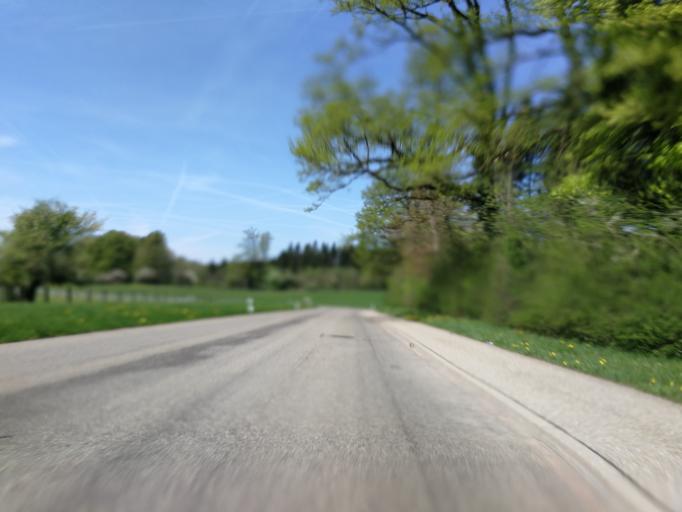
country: CH
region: Zurich
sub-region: Bezirk Hinwil
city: Hinwil
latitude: 47.2917
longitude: 8.8228
